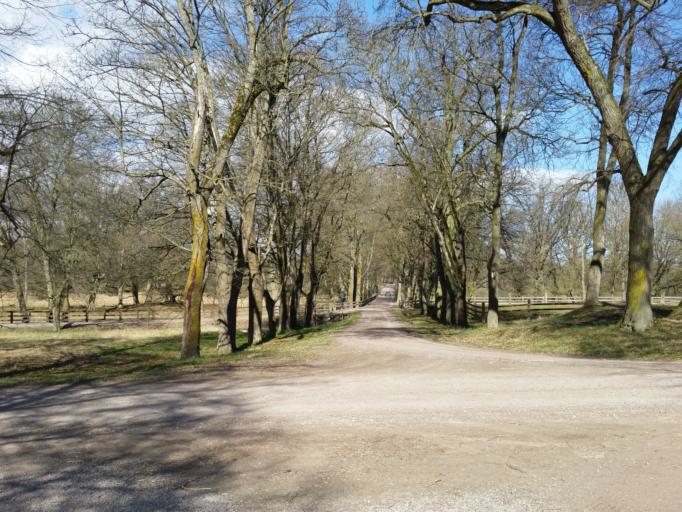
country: SE
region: Kalmar
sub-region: Monsteras Kommun
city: Timmernabben
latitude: 56.9364
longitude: 16.4244
